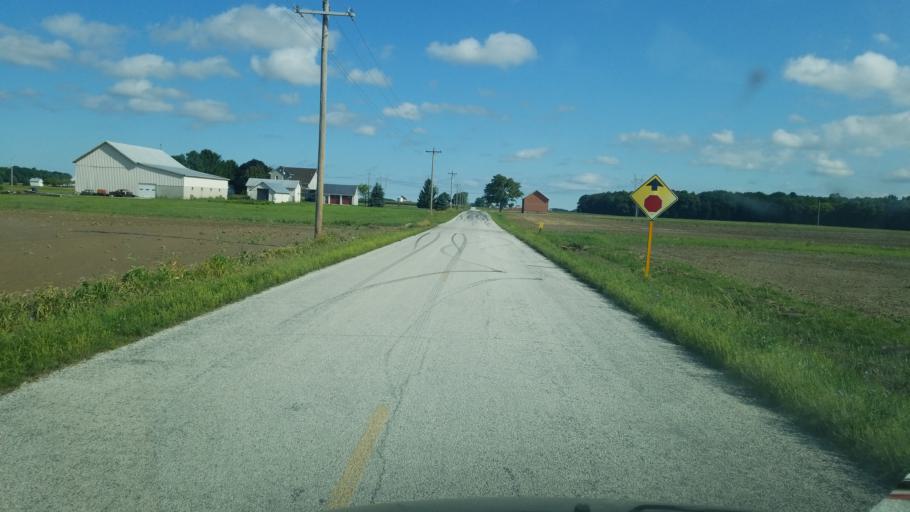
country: US
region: Ohio
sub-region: Seneca County
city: Fostoria
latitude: 41.0625
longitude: -83.3632
